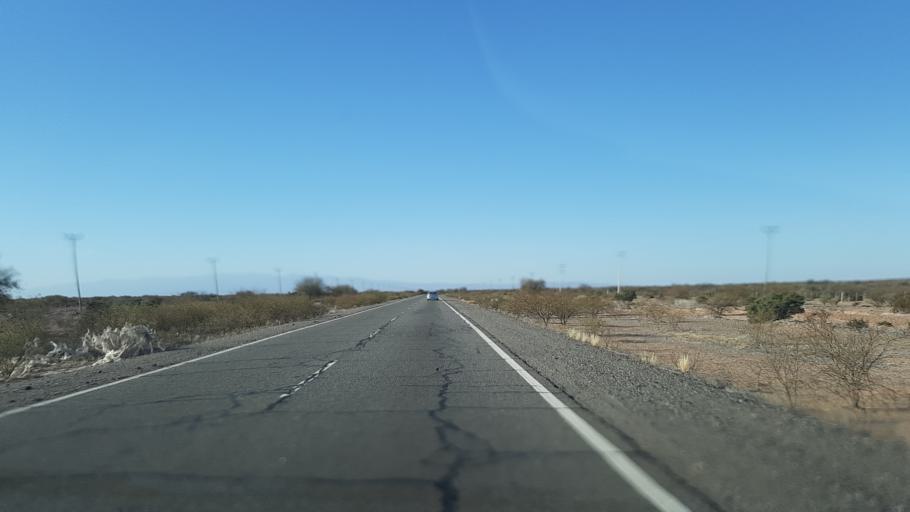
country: AR
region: San Juan
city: Caucete
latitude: -31.6345
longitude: -67.7476
